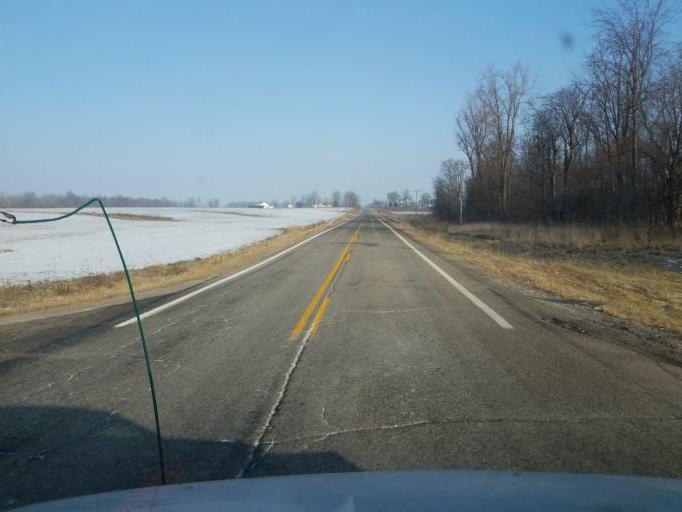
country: US
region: Ohio
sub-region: Crawford County
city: Galion
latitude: 40.6757
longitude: -82.8609
